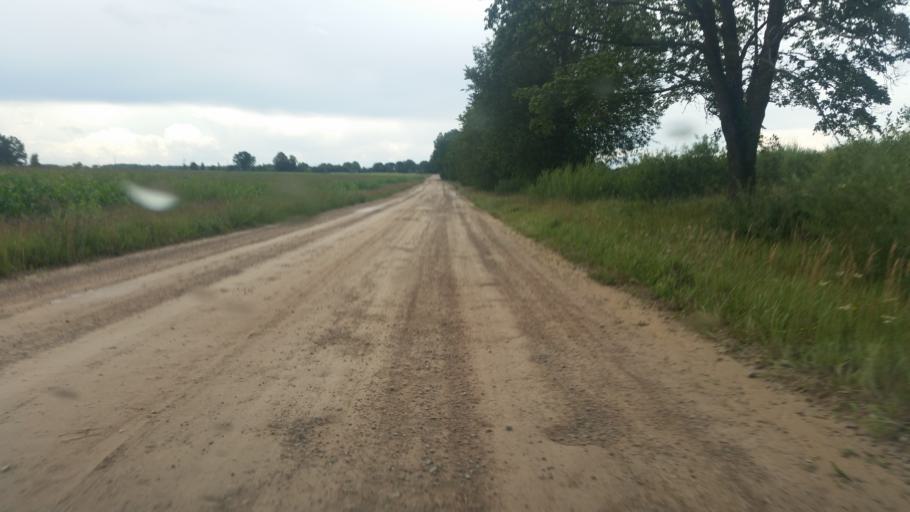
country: LV
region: Vecumnieki
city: Vecumnieki
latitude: 56.4552
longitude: 24.6032
